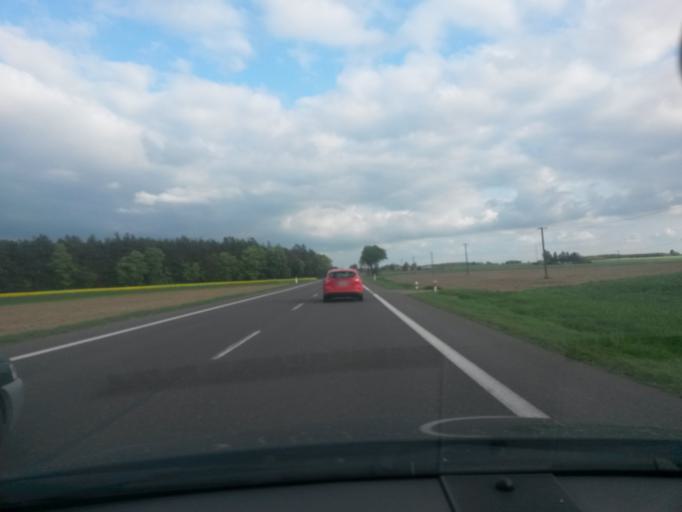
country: PL
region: Masovian Voivodeship
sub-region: Powiat plocki
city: Starozreby
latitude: 52.6625
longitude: 20.0768
